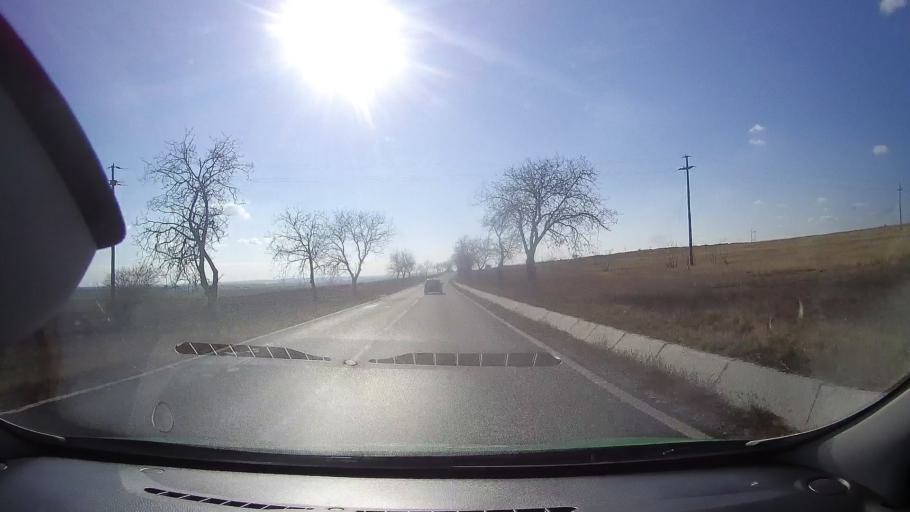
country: RO
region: Tulcea
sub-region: Comuna Ceamurlia de Jos
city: Ceamurlia de Jos
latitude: 44.8096
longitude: 28.6913
